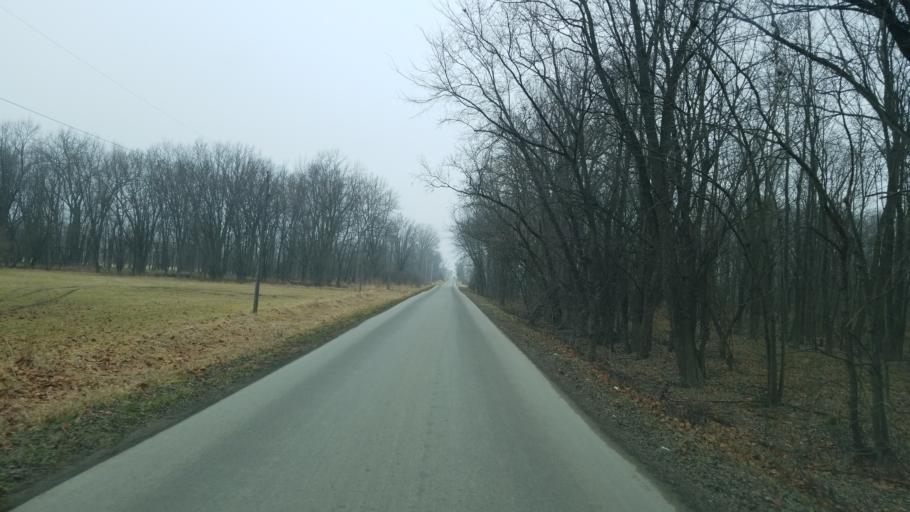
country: US
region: Indiana
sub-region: Adams County
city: Geneva
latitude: 40.5698
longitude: -84.8492
